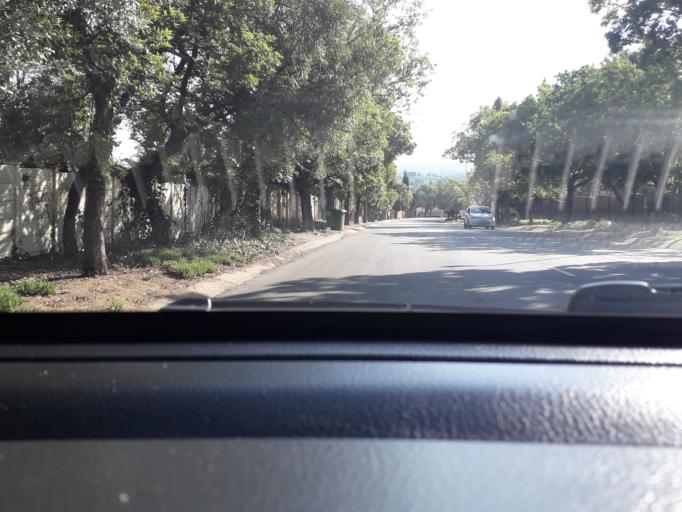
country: ZA
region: Gauteng
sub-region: City of Johannesburg Metropolitan Municipality
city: Midrand
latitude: -26.0388
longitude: 28.0768
